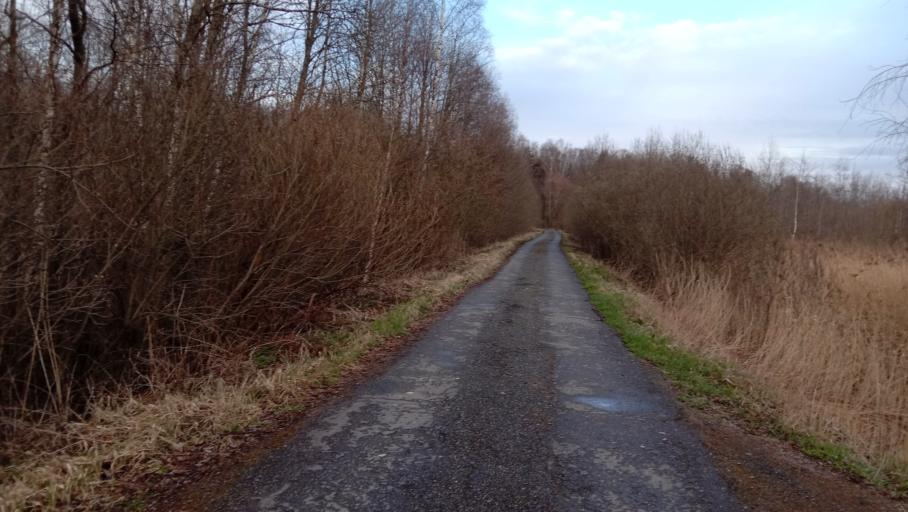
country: RU
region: Moskovskaya
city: Uvarovka
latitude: 55.7636
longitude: 35.7864
